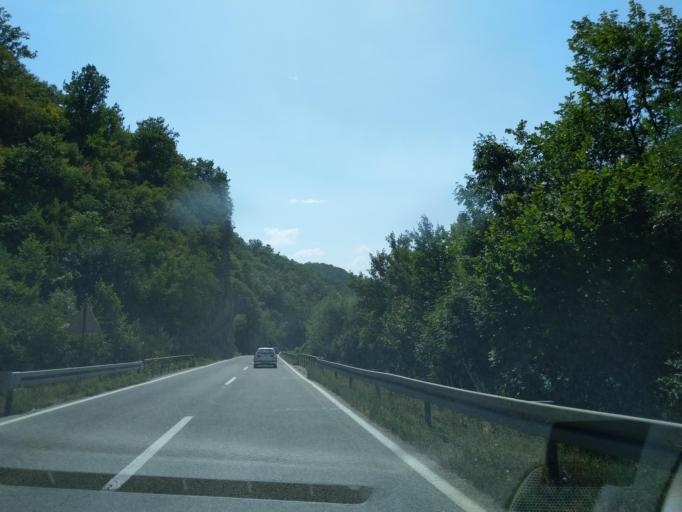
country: RS
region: Central Serbia
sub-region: Zlatiborski Okrug
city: Prijepolje
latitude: 43.4620
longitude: 19.6469
